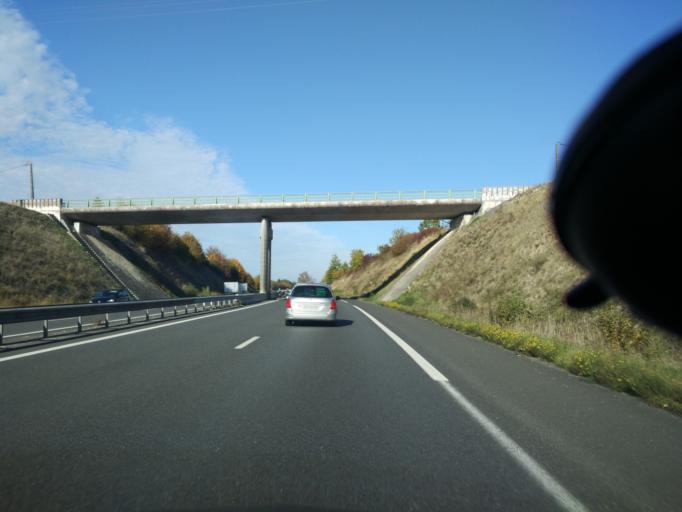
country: FR
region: Poitou-Charentes
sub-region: Departement de la Charente
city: Barbezieux-Saint-Hilaire
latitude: 45.4679
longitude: -0.1335
